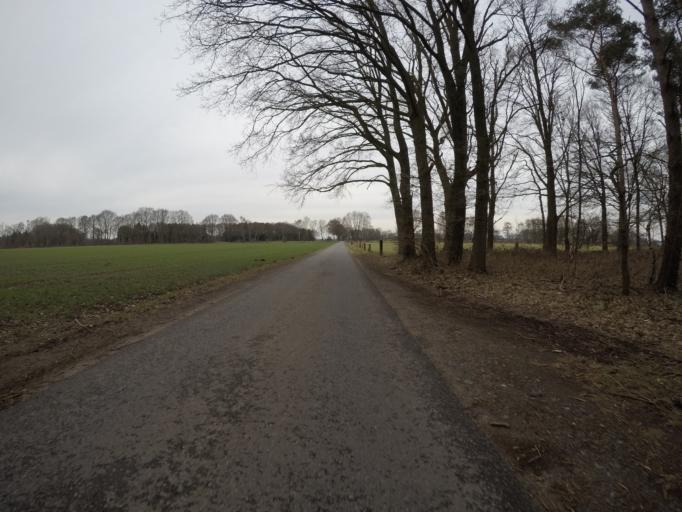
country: DE
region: North Rhine-Westphalia
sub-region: Regierungsbezirk Dusseldorf
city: Bocholt
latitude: 51.8040
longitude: 6.6288
